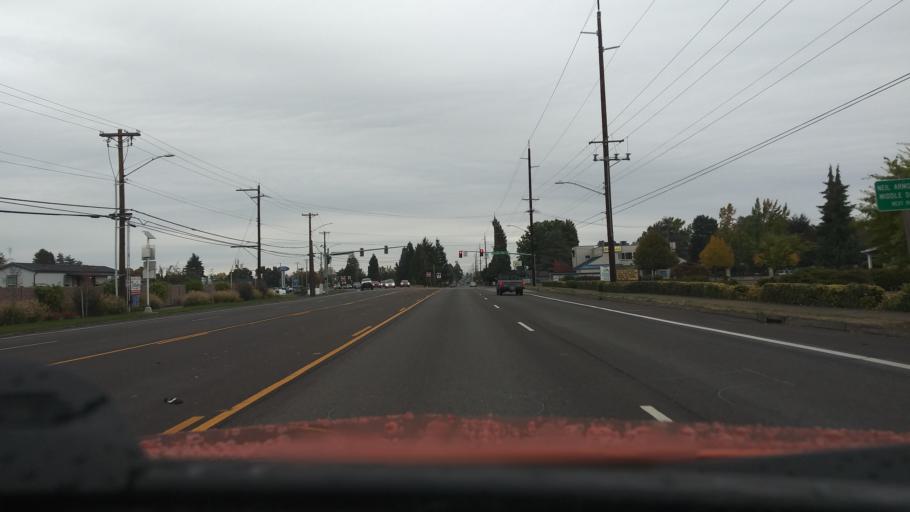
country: US
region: Oregon
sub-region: Washington County
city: Cornelius
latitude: 45.5202
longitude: -123.0774
